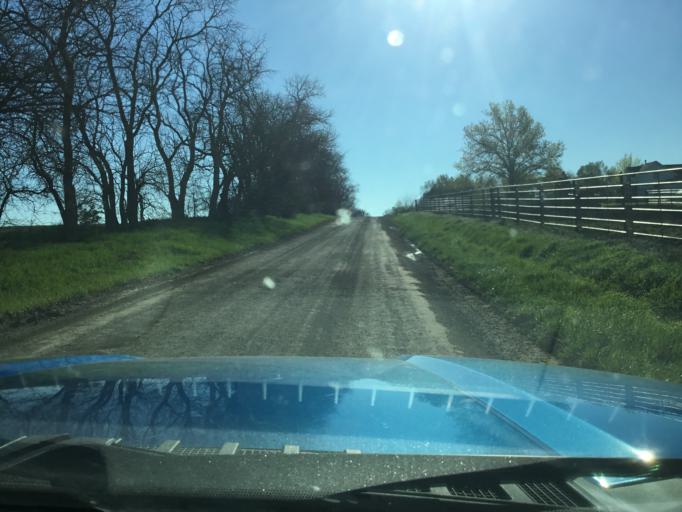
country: US
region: Kansas
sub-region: Douglas County
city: Lawrence
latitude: 38.9569
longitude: -95.3681
